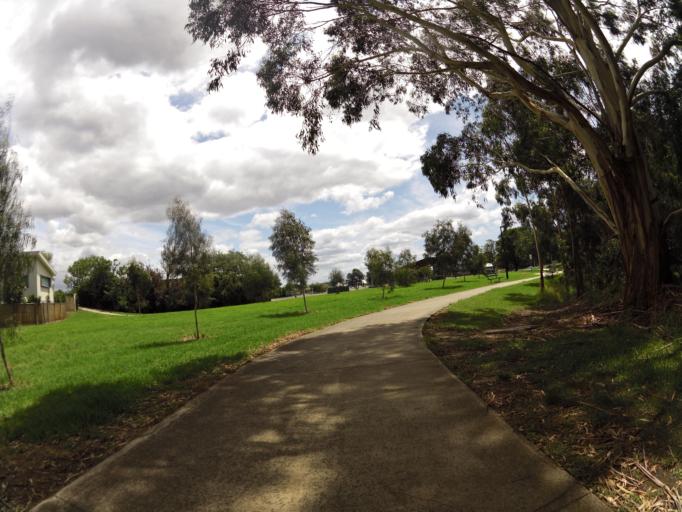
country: AU
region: Victoria
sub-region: Latrobe
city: Traralgon
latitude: -38.1900
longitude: 146.5368
